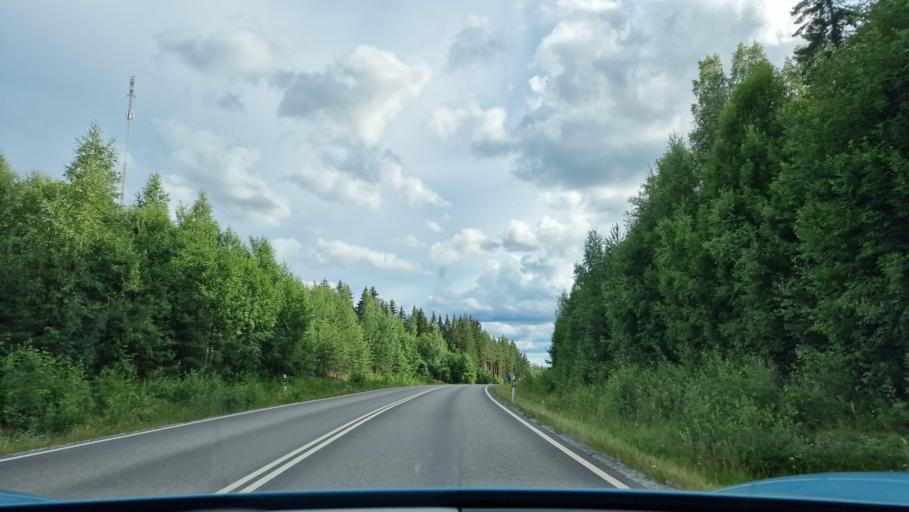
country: FI
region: Pirkanmaa
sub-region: Tampere
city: Paelkaene
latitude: 61.2545
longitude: 24.2289
